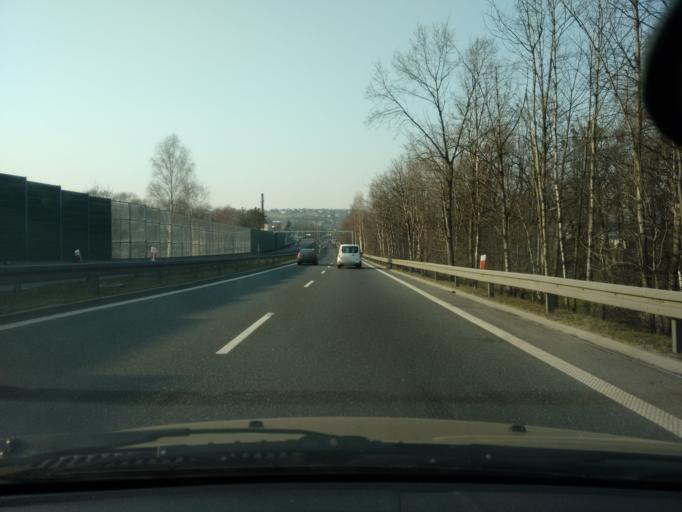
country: PL
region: Silesian Voivodeship
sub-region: Powiat cieszynski
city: Skoczow
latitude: 49.7984
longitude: 18.7935
